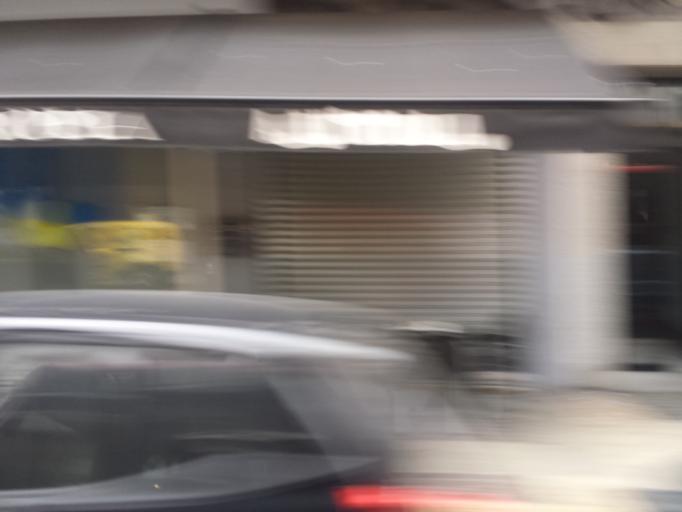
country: ES
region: Aragon
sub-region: Provincia de Zaragoza
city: Zaragoza
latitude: 41.6348
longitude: -0.8787
